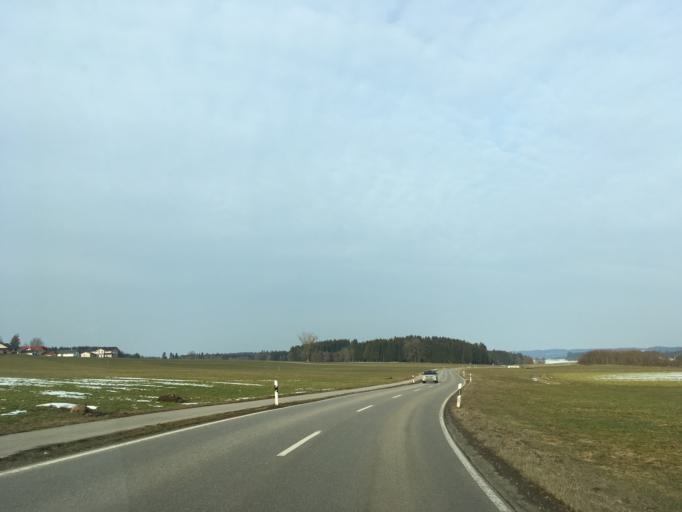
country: DE
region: Bavaria
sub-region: Upper Bavaria
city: Sochtenau
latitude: 47.9335
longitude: 12.2328
